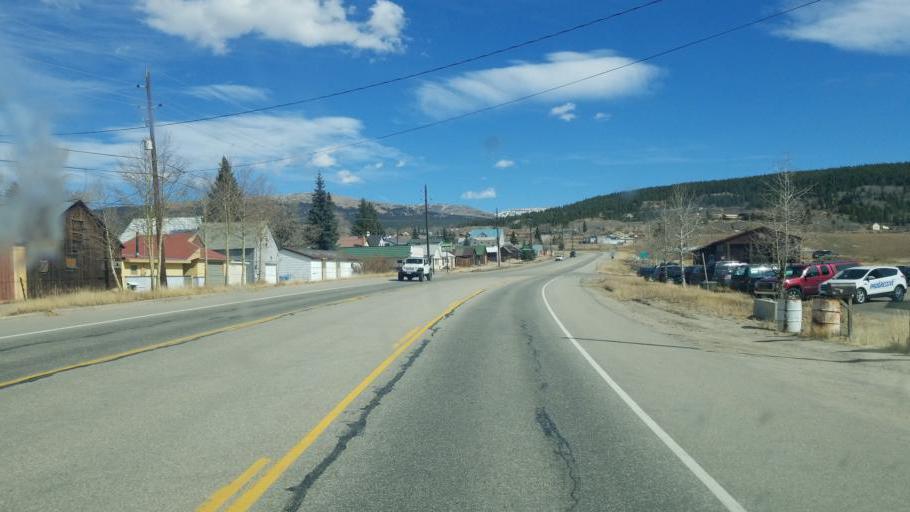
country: US
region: Colorado
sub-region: Lake County
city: Leadville
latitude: 39.2421
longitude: -106.2946
